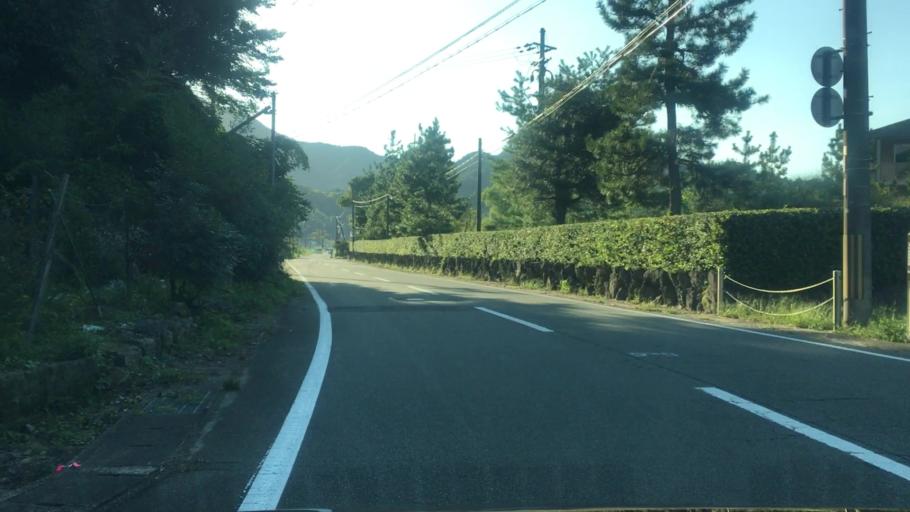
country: JP
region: Hyogo
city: Toyooka
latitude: 35.6191
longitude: 134.8207
